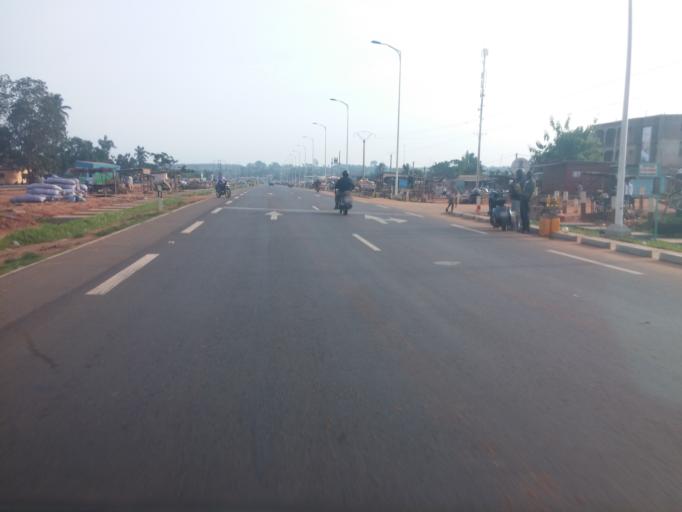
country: TG
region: Maritime
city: Tsevie
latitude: 6.3209
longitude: 1.2177
